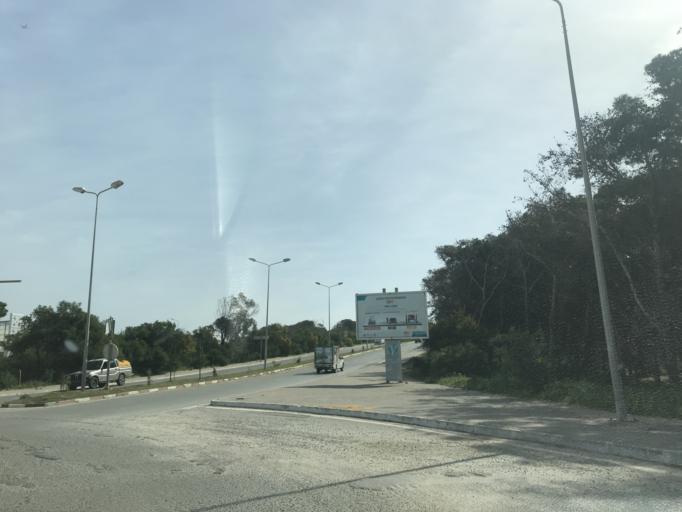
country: TN
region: Tunis
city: Al Marsa
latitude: 36.9196
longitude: 10.2910
